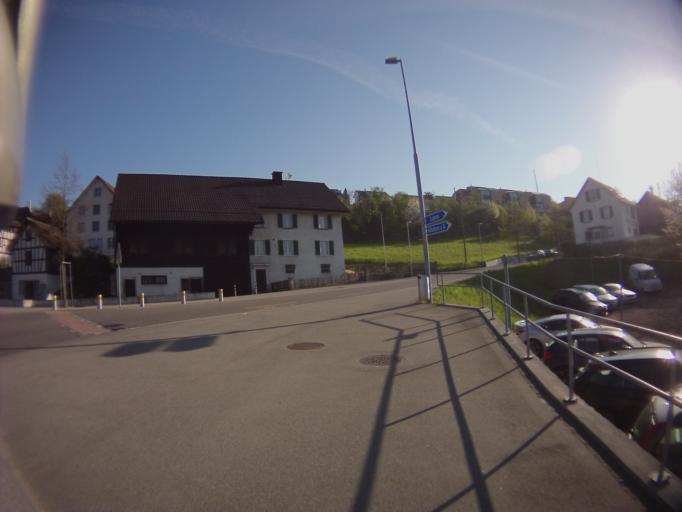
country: CH
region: Zurich
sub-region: Bezirk Dietikon
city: Birmensdorf
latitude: 47.3569
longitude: 8.4355
